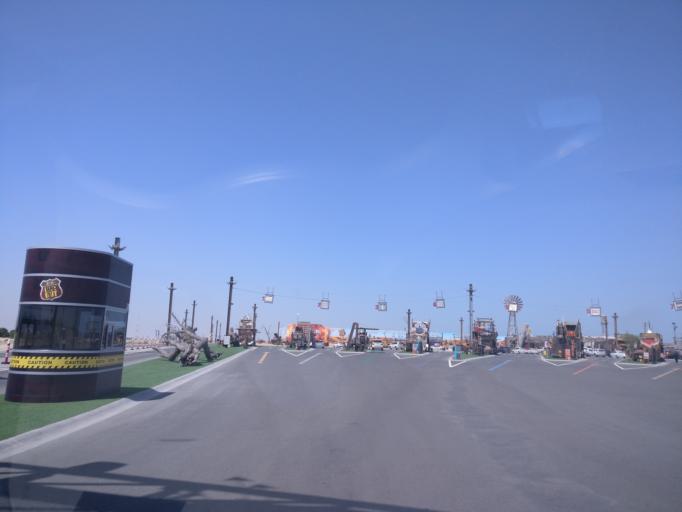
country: AE
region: Dubai
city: Dubai
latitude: 24.9138
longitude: 54.9623
